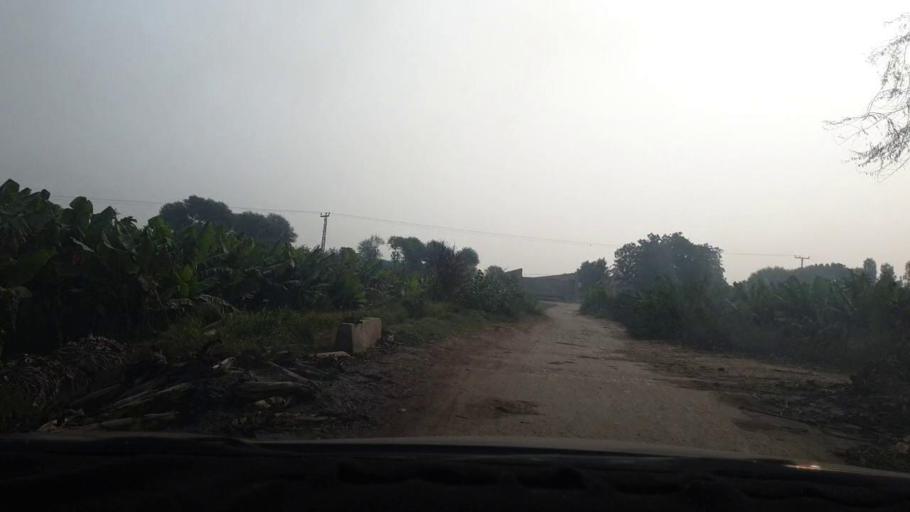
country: PK
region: Sindh
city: Matiari
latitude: 25.5913
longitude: 68.5480
